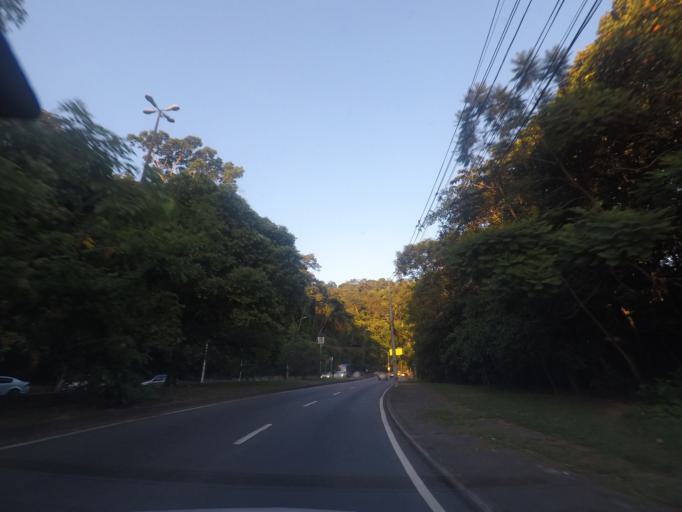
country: BR
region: Rio de Janeiro
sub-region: Rio De Janeiro
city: Rio de Janeiro
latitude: -22.9247
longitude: -43.3142
